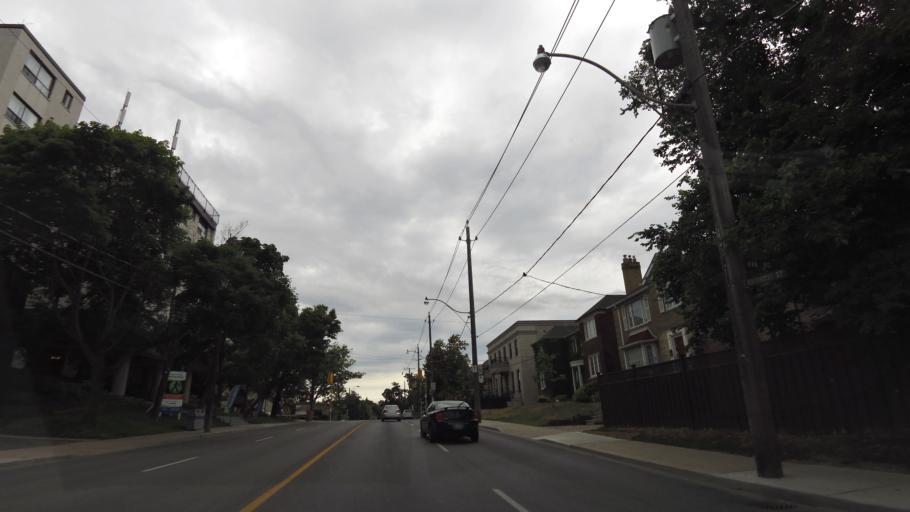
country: CA
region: Ontario
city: Toronto
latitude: 43.6973
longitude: -79.4240
